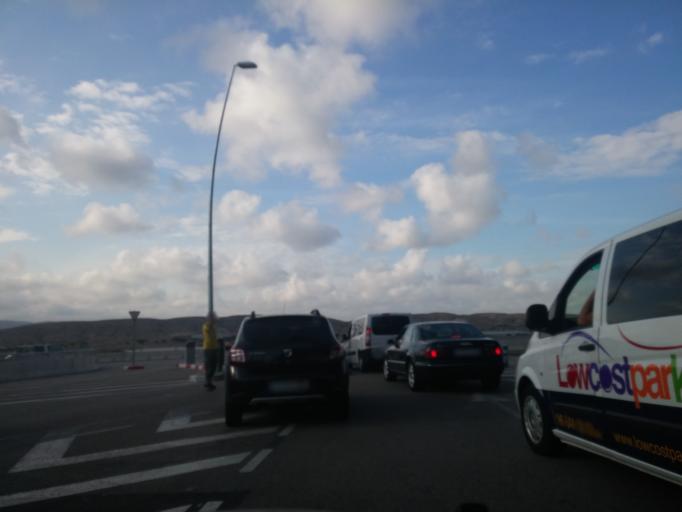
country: ES
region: Valencia
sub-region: Provincia de Alicante
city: Alicante
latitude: 38.2882
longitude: -0.5529
